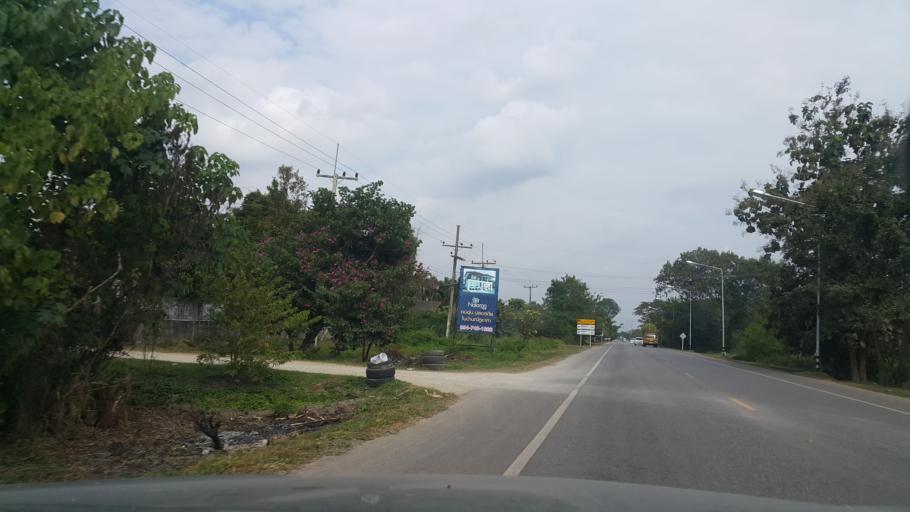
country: TH
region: Phayao
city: Phayao
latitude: 19.0915
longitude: 99.9051
